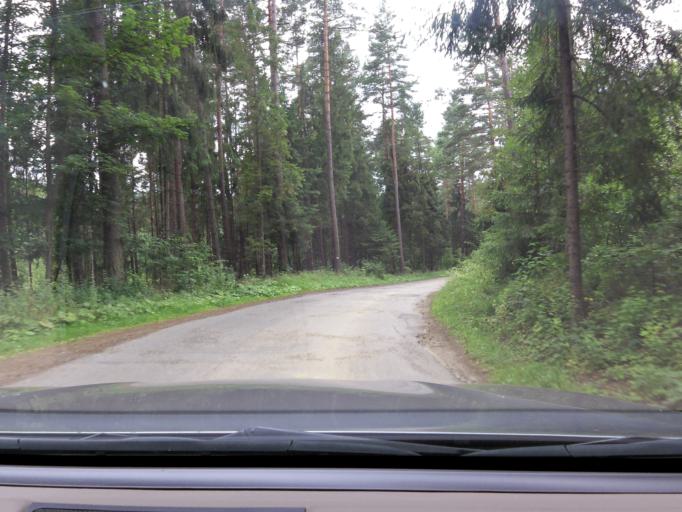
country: PL
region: Silesian Voivodeship
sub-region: Powiat zywiecki
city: Rajcza
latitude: 49.5014
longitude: 19.1296
